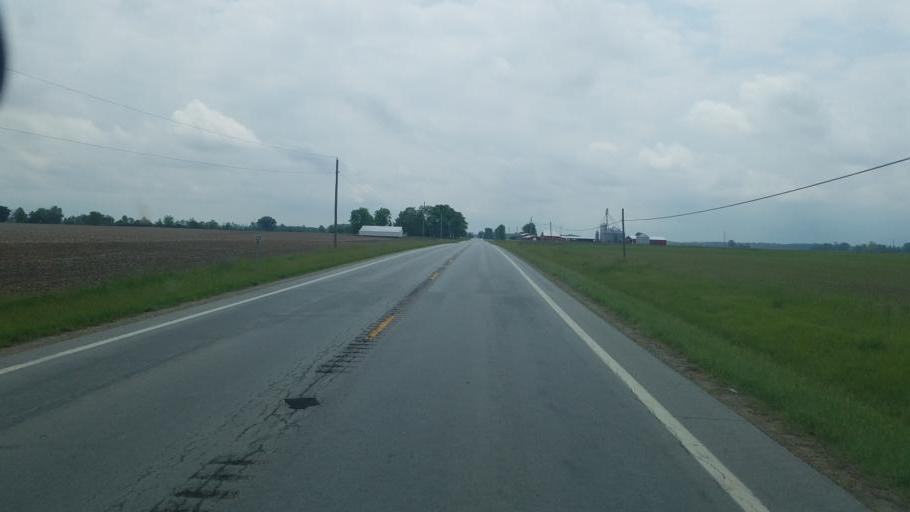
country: US
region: Ohio
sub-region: Union County
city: Richwood
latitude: 40.3410
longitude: -83.3090
